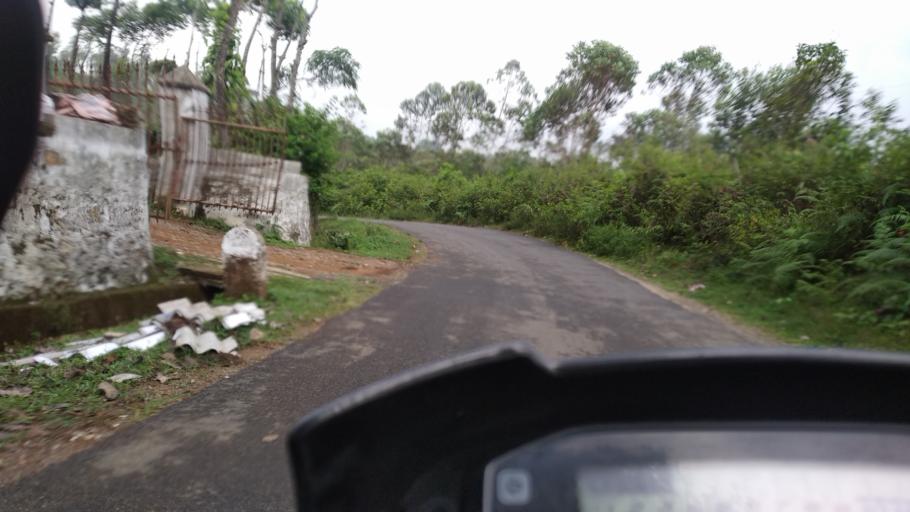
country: IN
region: Kerala
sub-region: Kottayam
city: Erattupetta
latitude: 9.5874
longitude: 77.0079
